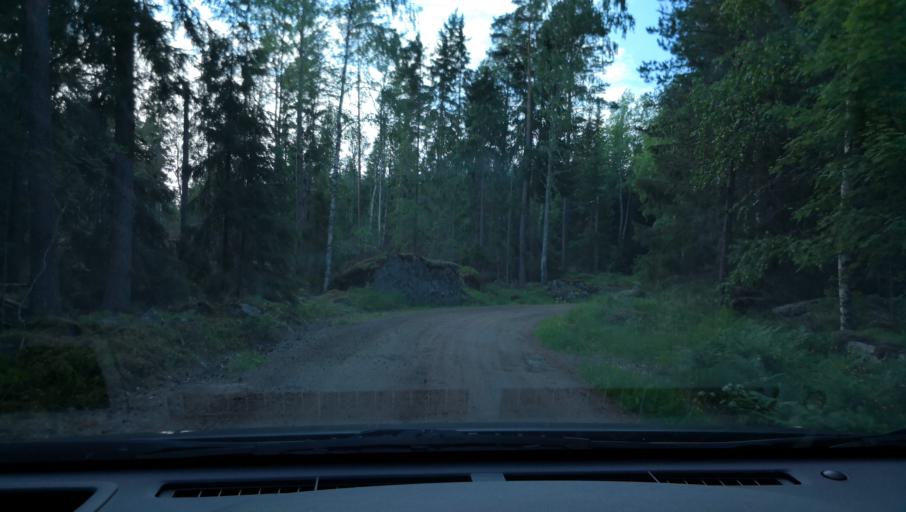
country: SE
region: Uppsala
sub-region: Enkopings Kommun
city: Orsundsbro
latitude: 59.8366
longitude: 17.2242
